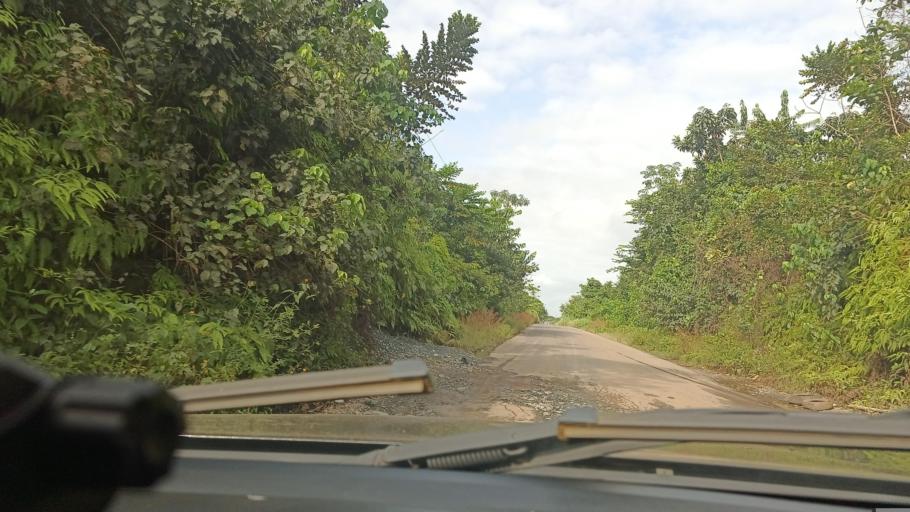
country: LR
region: Bomi
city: Tubmanburg
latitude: 6.7128
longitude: -10.9432
